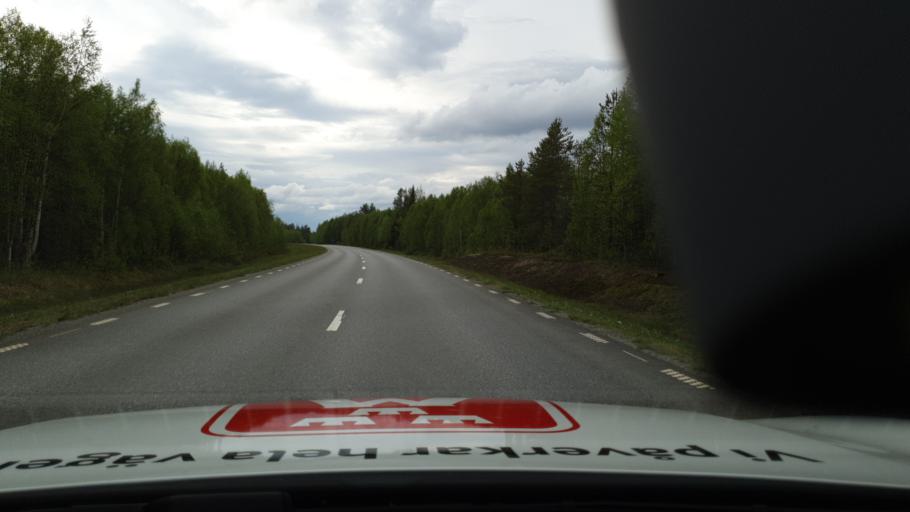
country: SE
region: Vaesterbotten
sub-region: Dorotea Kommun
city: Dorotea
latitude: 64.3480
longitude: 16.6592
